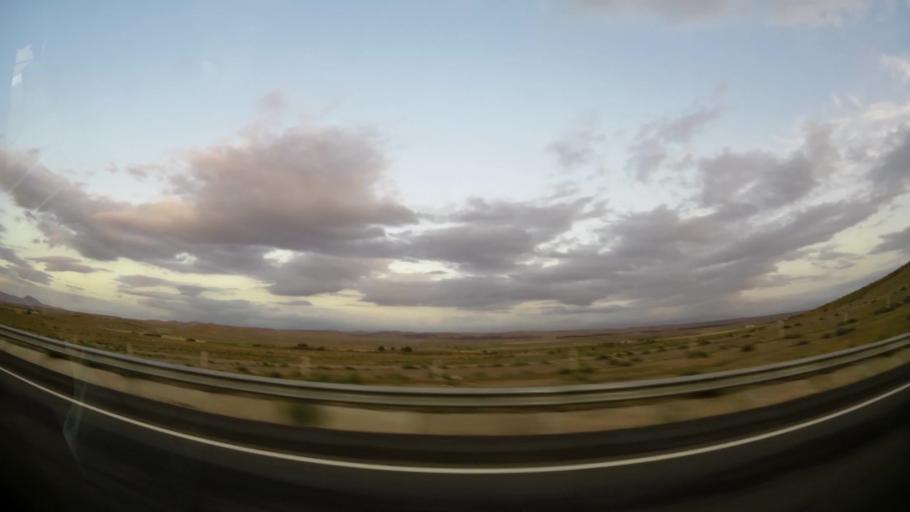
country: MA
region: Oriental
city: Taourirt
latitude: 34.5785
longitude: -2.8100
